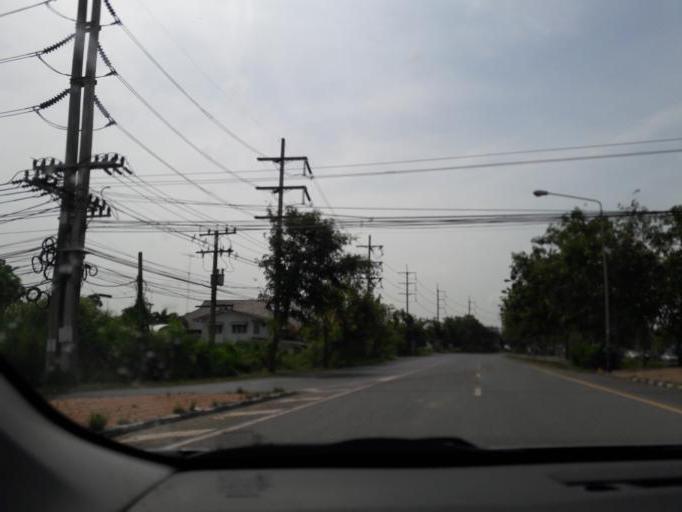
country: TH
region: Ang Thong
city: Ang Thong
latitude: 14.5807
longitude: 100.4627
